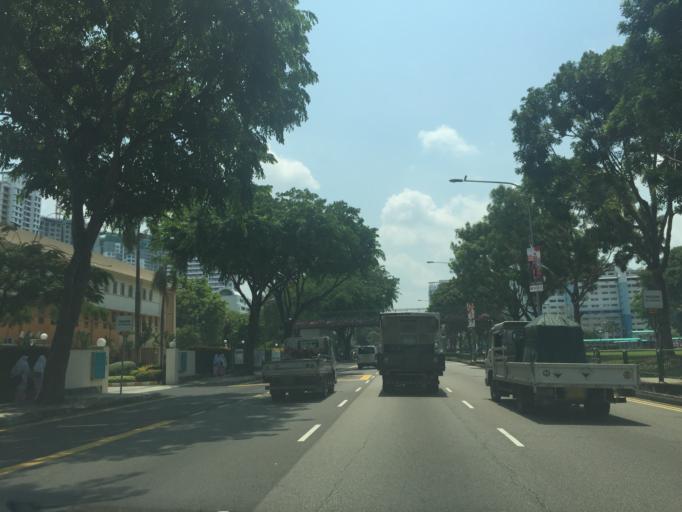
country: SG
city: Singapore
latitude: 1.3168
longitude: 103.8593
